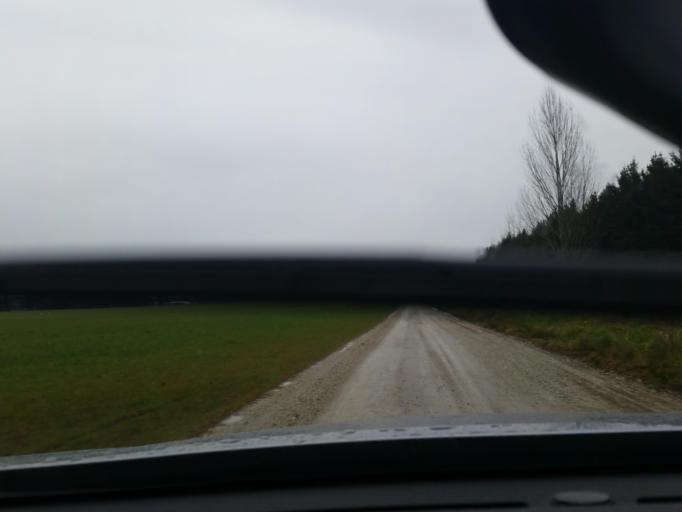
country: NZ
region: Southland
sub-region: Southland District
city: Winton
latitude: -46.2281
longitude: 168.4884
